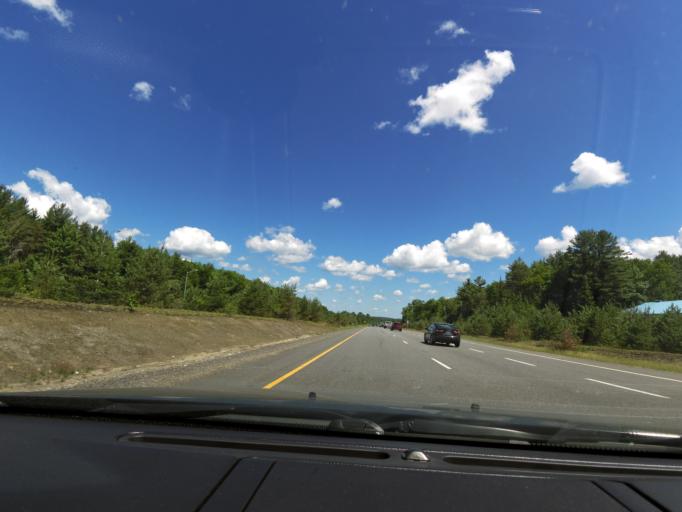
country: CA
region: Ontario
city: Huntsville
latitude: 45.2160
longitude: -79.3136
